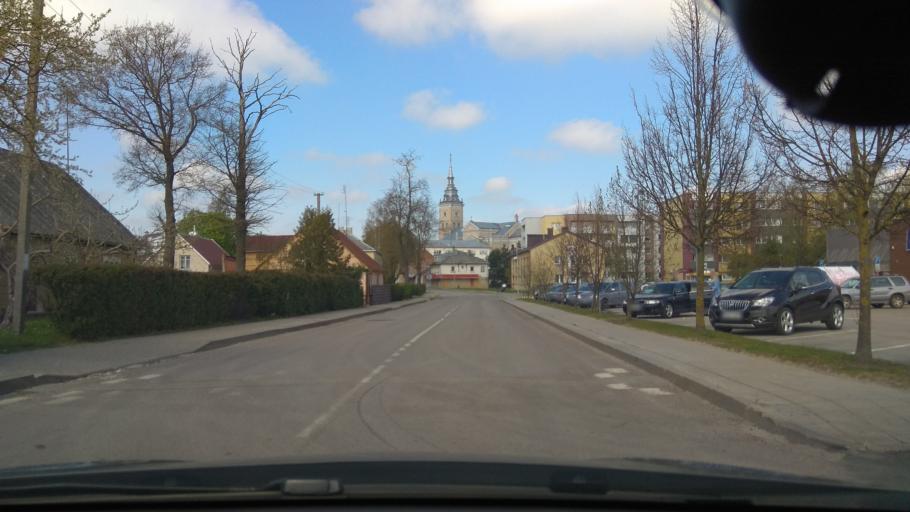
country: LT
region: Siauliu apskritis
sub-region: Joniskis
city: Joniskis
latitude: 56.2392
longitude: 23.6198
